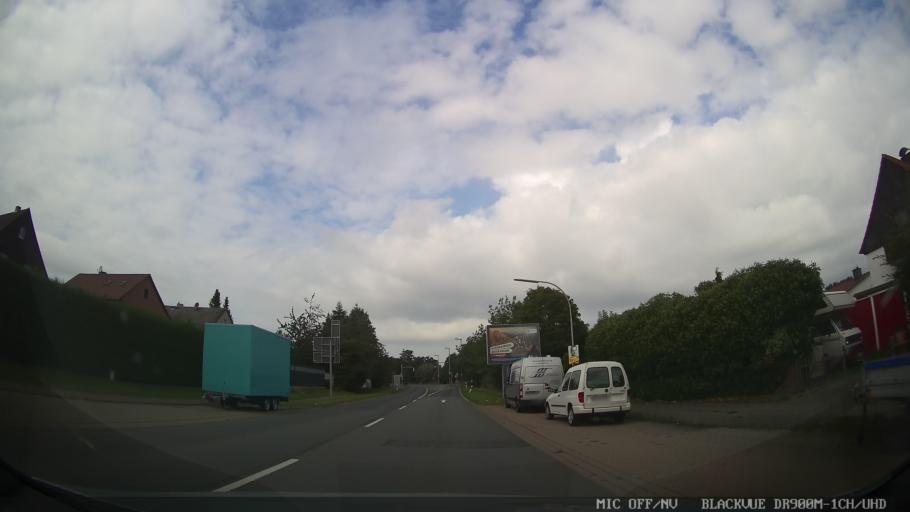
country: DE
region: Lower Saxony
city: Klein Schwulper
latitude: 52.3078
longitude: 10.4623
